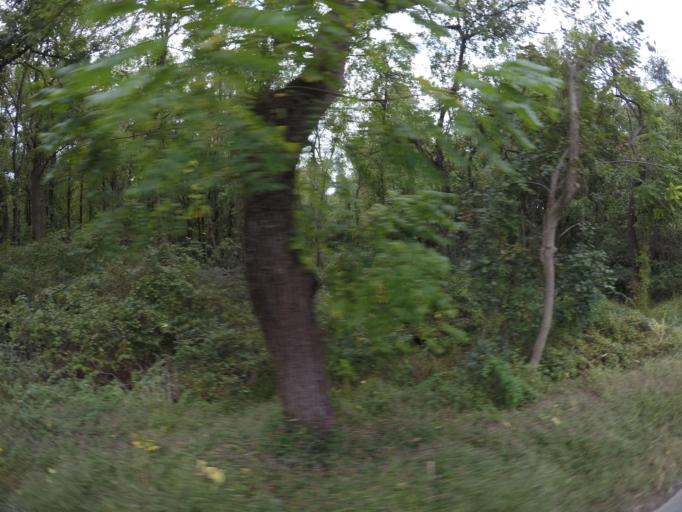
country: US
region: Delaware
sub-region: New Castle County
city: Newark
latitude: 39.7205
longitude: -75.7773
